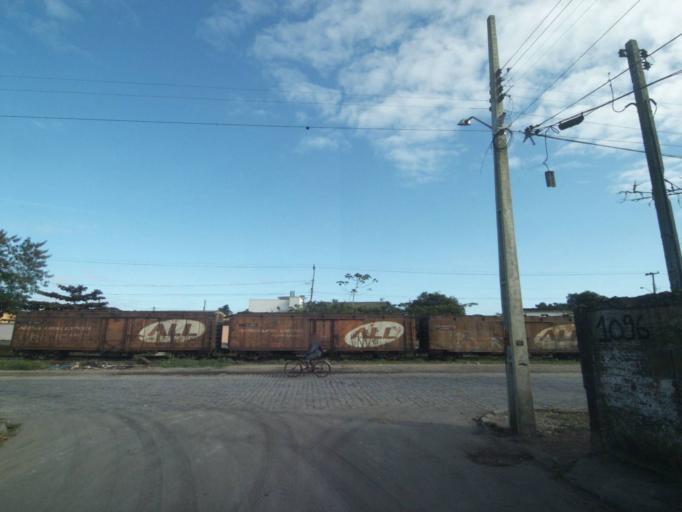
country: BR
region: Parana
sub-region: Paranagua
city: Paranagua
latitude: -25.5235
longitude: -48.5281
